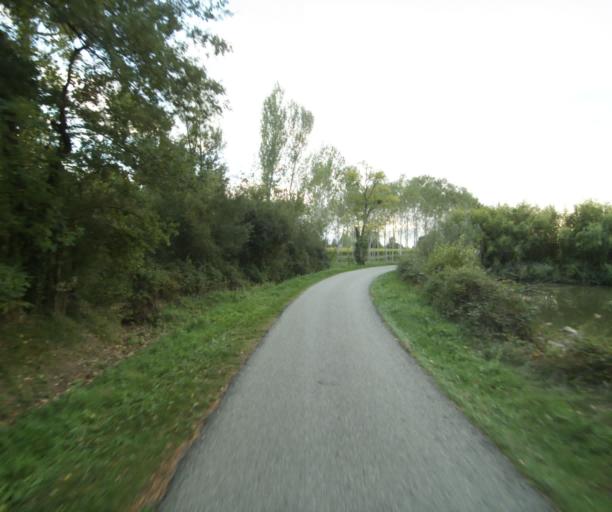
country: FR
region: Aquitaine
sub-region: Departement des Landes
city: Gabarret
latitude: 43.9740
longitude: 0.0997
